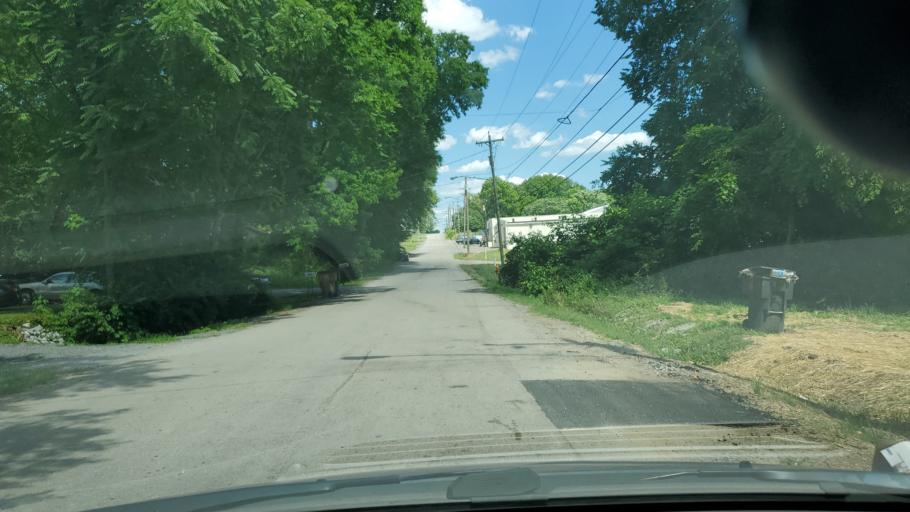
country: US
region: Tennessee
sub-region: Davidson County
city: Nashville
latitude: 36.2021
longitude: -86.7573
